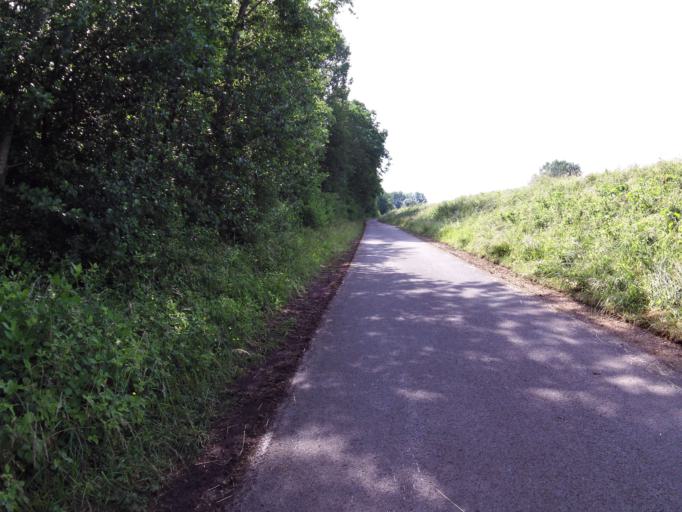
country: FR
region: Champagne-Ardenne
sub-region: Departement de l'Aube
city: Verrieres
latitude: 48.2693
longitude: 4.1701
